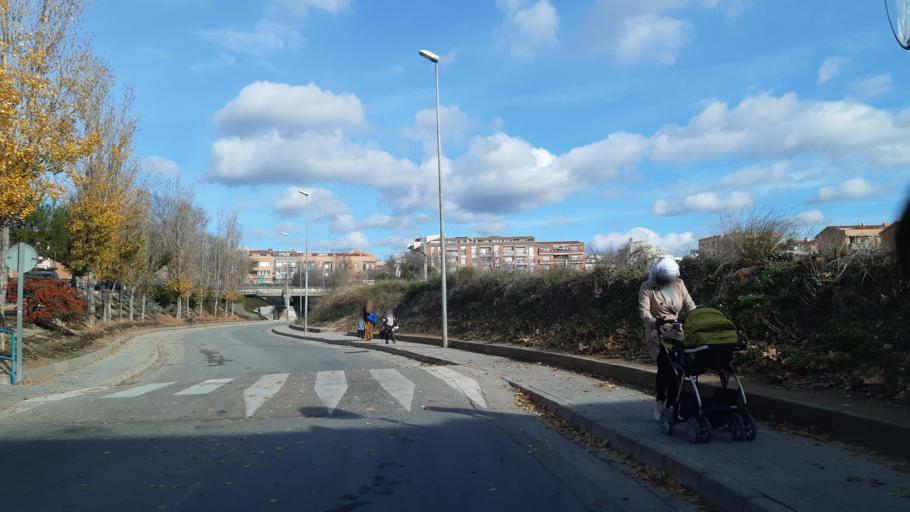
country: ES
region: Catalonia
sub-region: Provincia de Barcelona
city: Vilanova del Cami
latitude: 41.5706
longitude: 1.6441
